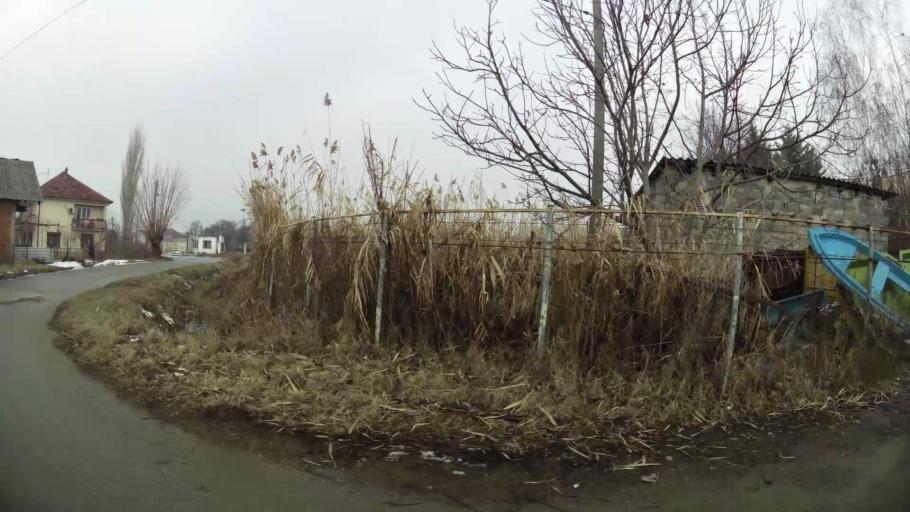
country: MK
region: Ilinden
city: Ilinden
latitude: 41.9906
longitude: 21.5763
